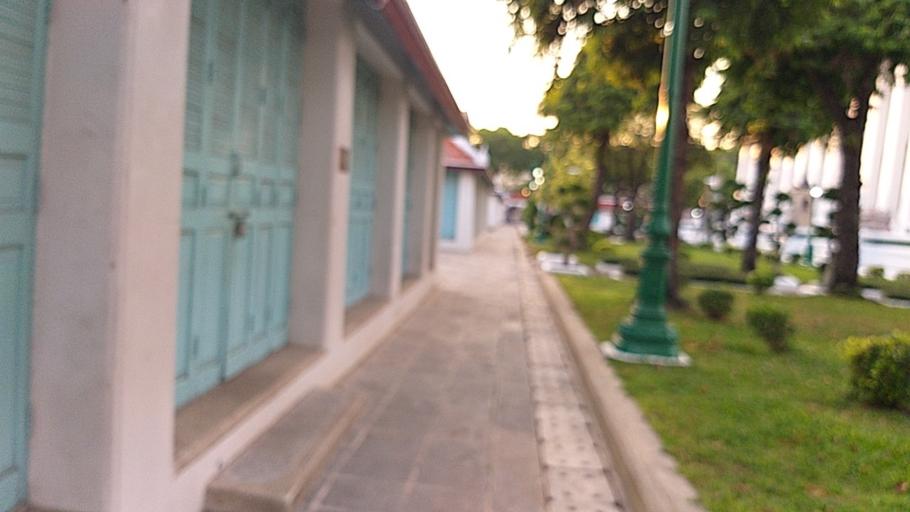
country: TH
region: Bangkok
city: Bangkok
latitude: 13.7499
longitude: 100.5014
